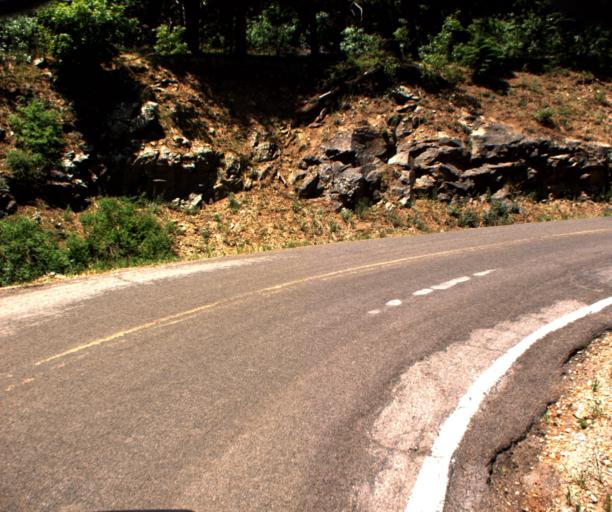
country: US
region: Arizona
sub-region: Graham County
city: Swift Trail Junction
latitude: 32.6267
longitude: -109.8246
